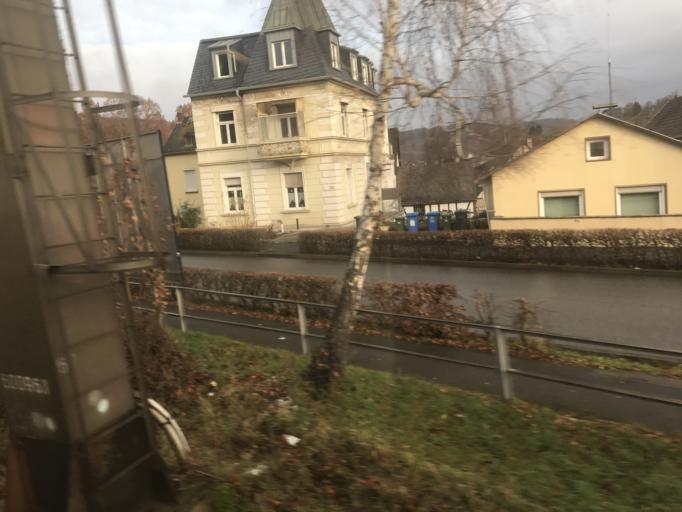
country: DE
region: Rheinland-Pfalz
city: Filsen
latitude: 50.2327
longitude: 7.5809
